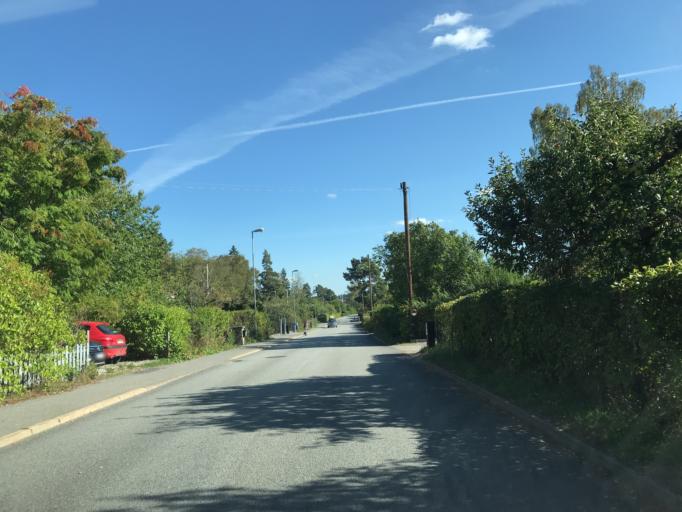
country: SE
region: Stockholm
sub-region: Sollentuna Kommun
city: Sollentuna
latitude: 59.4180
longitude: 17.9767
